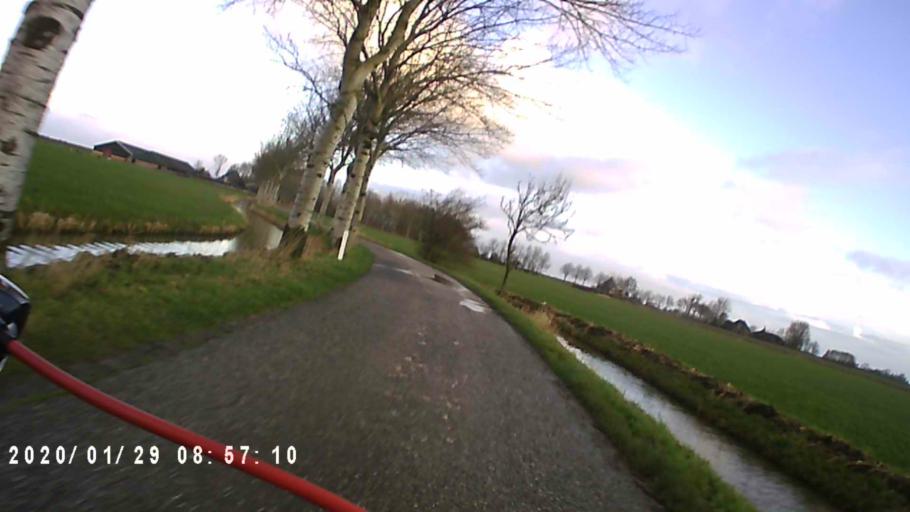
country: NL
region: Groningen
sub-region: Gemeente Zuidhorn
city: Aduard
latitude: 53.3151
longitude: 6.4551
